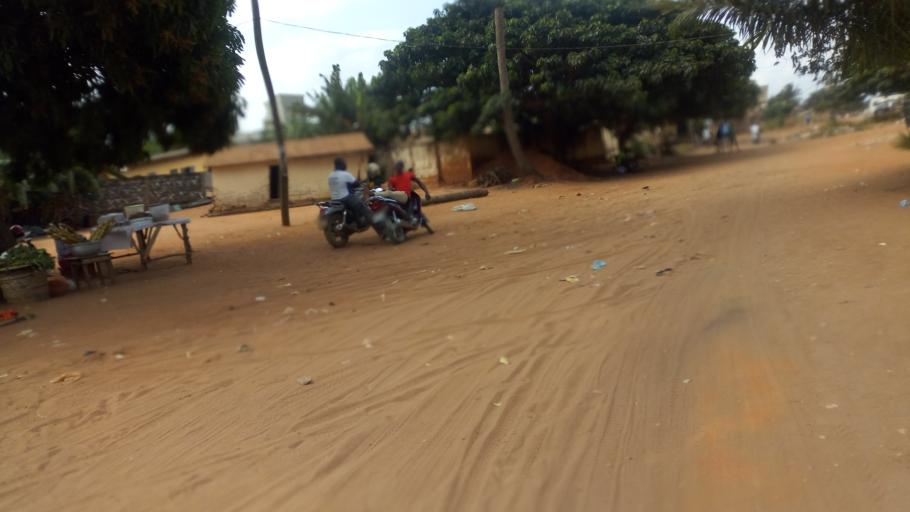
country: TG
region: Maritime
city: Lome
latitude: 6.2296
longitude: 1.1825
